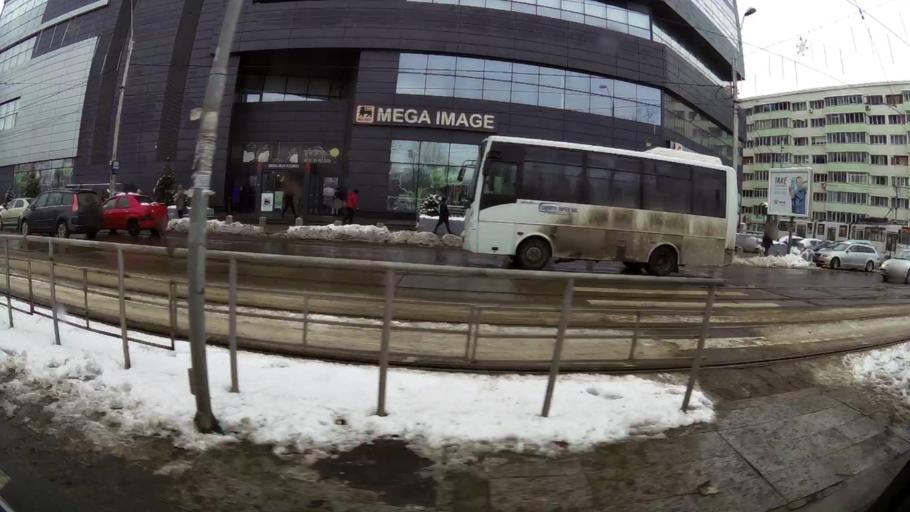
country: RO
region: Bucuresti
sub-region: Municipiul Bucuresti
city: Bucuresti
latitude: 44.4015
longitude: 26.0973
